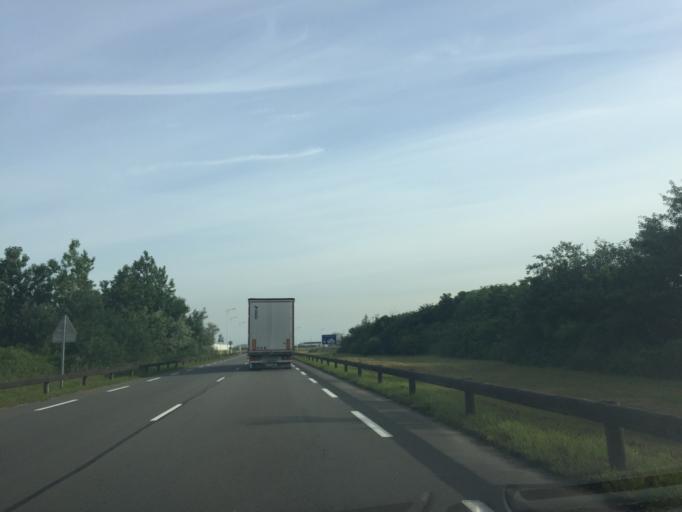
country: FR
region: Nord-Pas-de-Calais
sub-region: Departement du Nord
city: Loon-Plage
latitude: 51.0090
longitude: 2.1968
